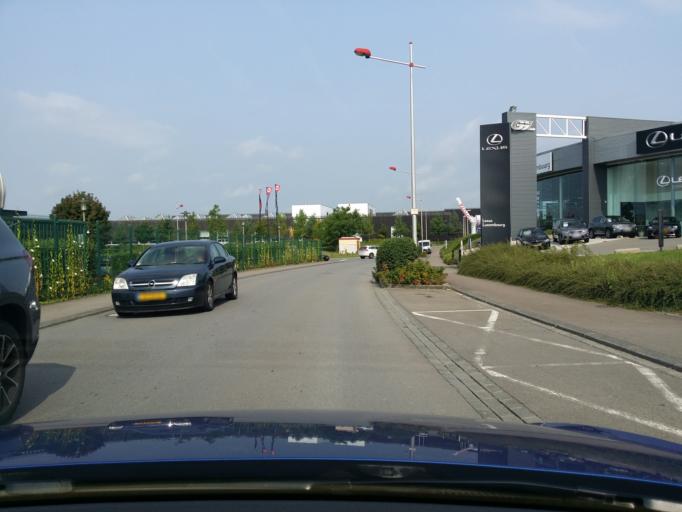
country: LU
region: Luxembourg
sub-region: Canton de Luxembourg
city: Strassen
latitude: 49.6085
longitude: 6.0771
